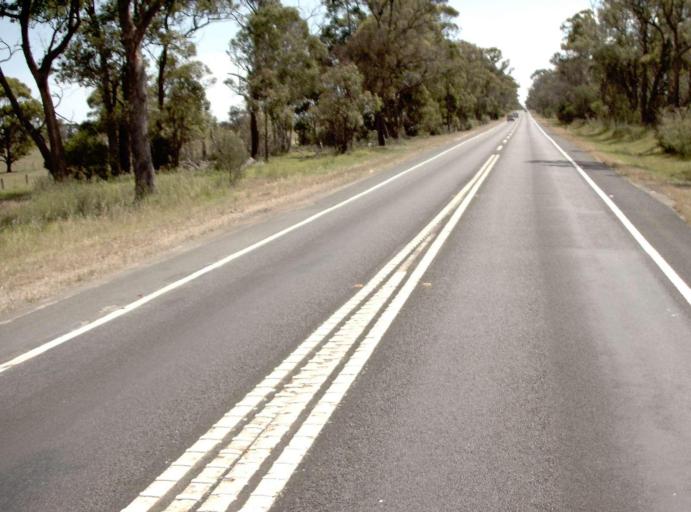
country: AU
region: Victoria
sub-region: Wellington
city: Sale
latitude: -37.9333
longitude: 147.1810
